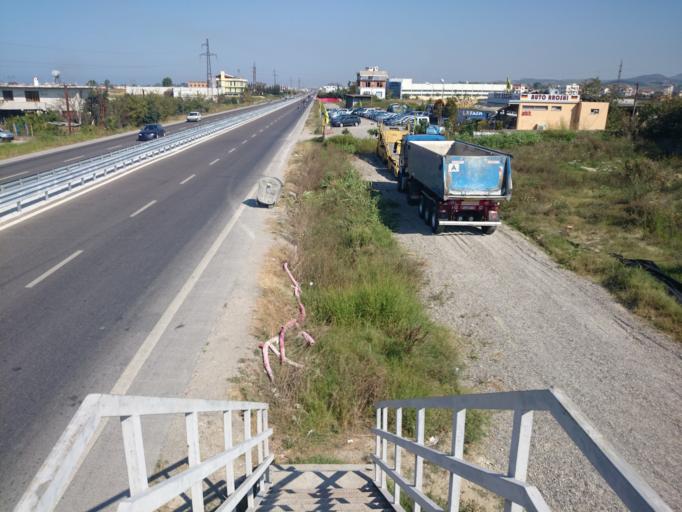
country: AL
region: Tirane
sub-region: Rrethi i Kavajes
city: Synej
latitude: 41.1880
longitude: 19.5419
